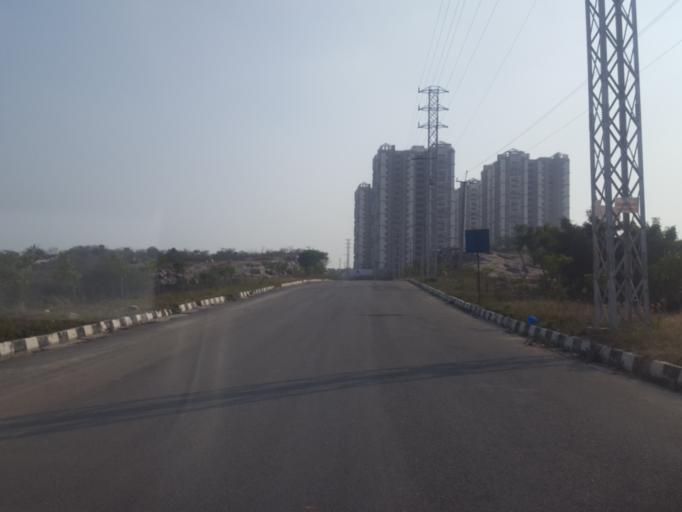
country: IN
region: Telangana
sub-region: Medak
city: Serilingampalle
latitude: 17.4105
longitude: 78.3151
